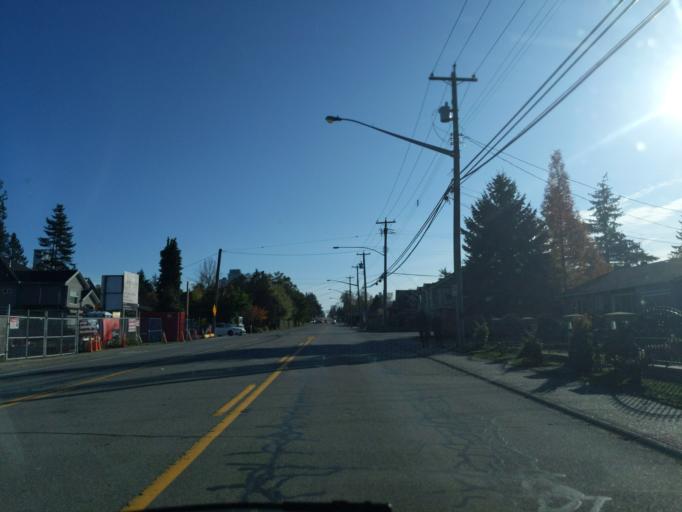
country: CA
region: British Columbia
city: New Westminster
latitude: 49.2013
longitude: -122.8565
